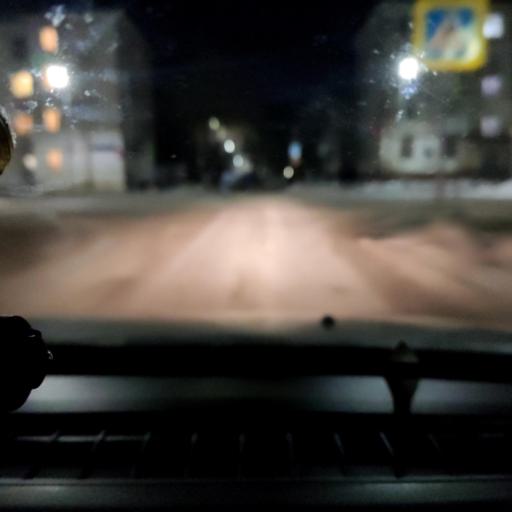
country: RU
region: Samara
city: Novokuybyshevsk
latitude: 53.0951
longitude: 49.9463
